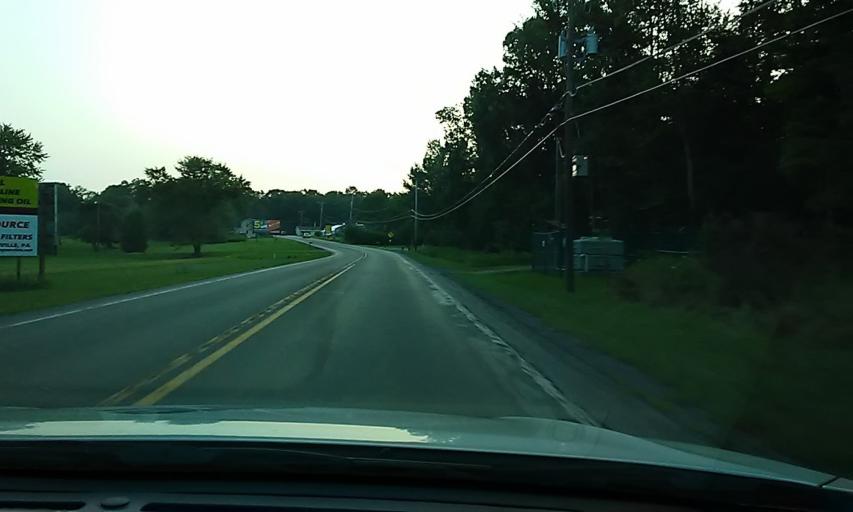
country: US
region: Pennsylvania
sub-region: Clarion County
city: Marianne
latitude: 41.2519
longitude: -79.4109
